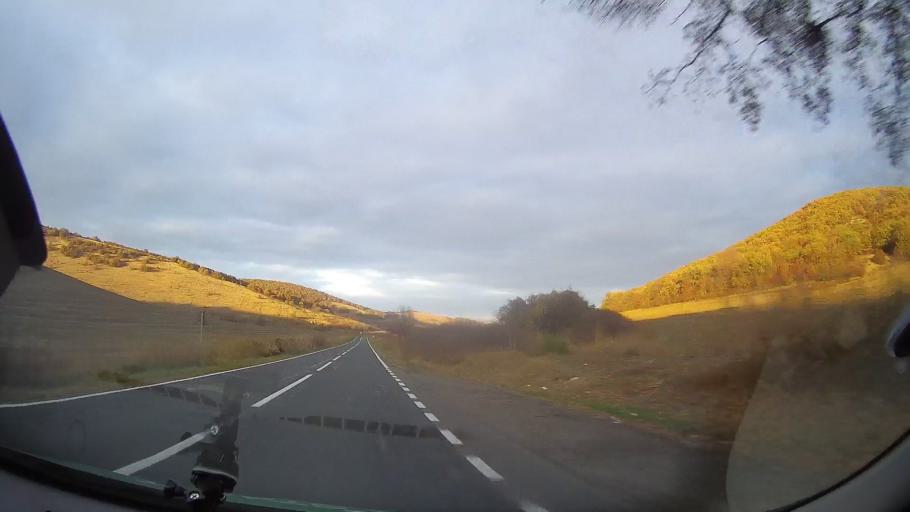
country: RO
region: Tulcea
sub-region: Comuna Ciucurova
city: Ciucurova
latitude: 44.9585
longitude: 28.5179
